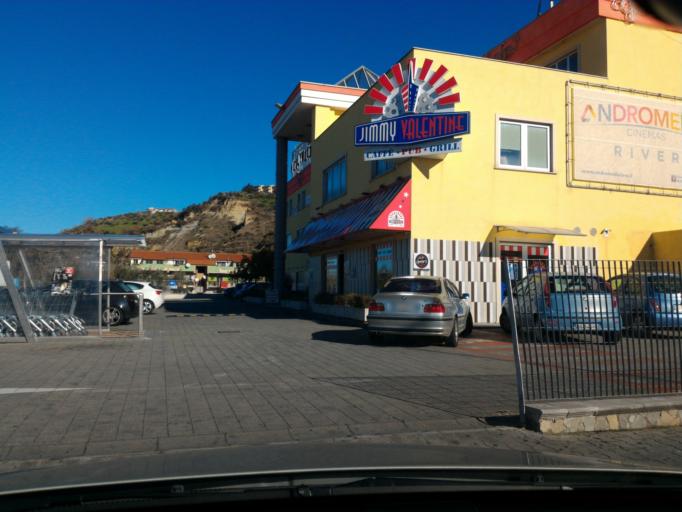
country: IT
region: Calabria
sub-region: Provincia di Cosenza
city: Cosenza
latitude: 39.3146
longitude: 16.2631
